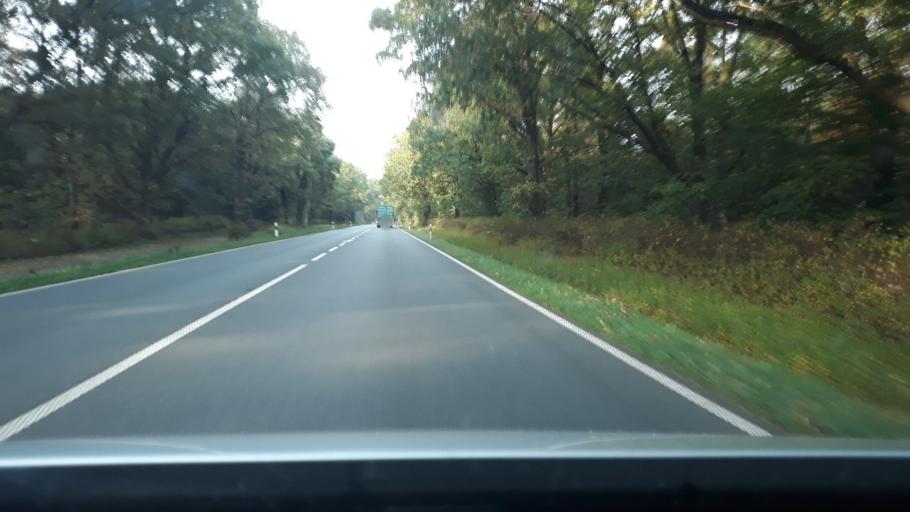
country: DE
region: Schleswig-Holstein
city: Kropp
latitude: 54.3976
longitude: 9.5374
